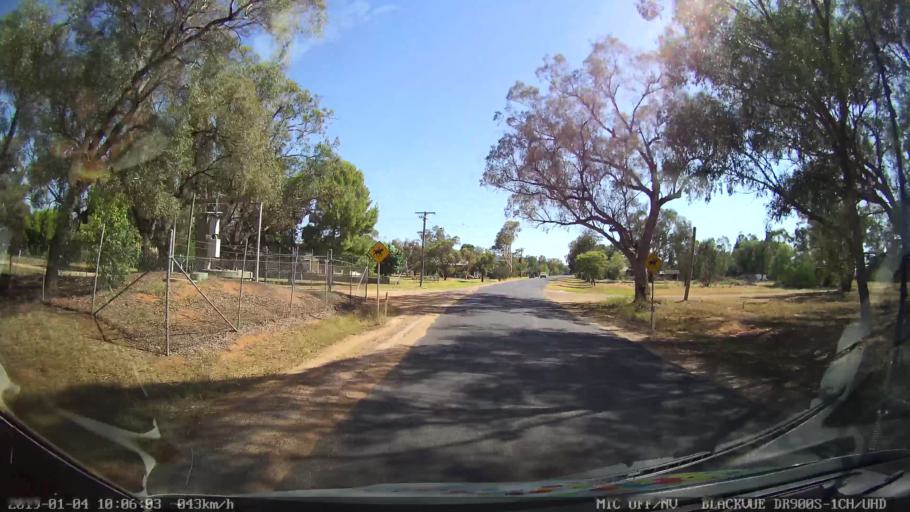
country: AU
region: New South Wales
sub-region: Cabonne
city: Canowindra
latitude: -33.4359
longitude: 148.3671
